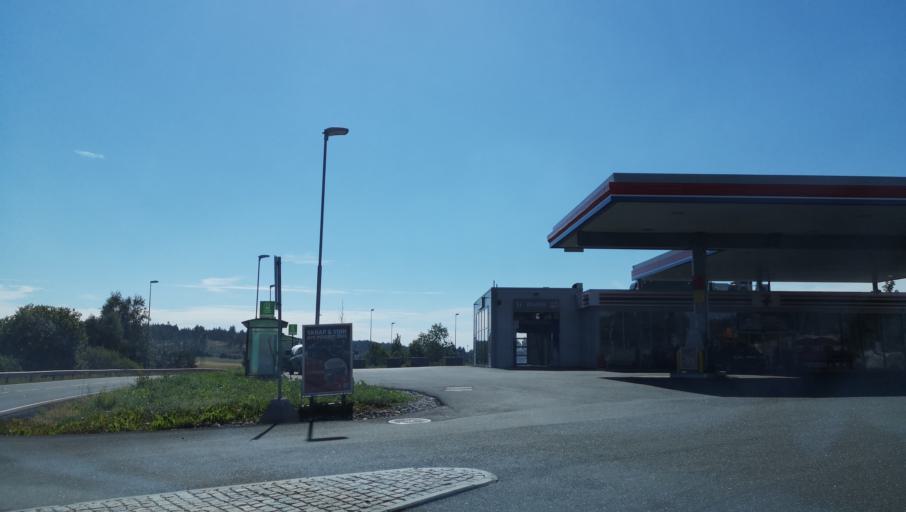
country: NO
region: Akershus
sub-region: Vestby
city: Vestby
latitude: 59.5156
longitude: 10.7281
